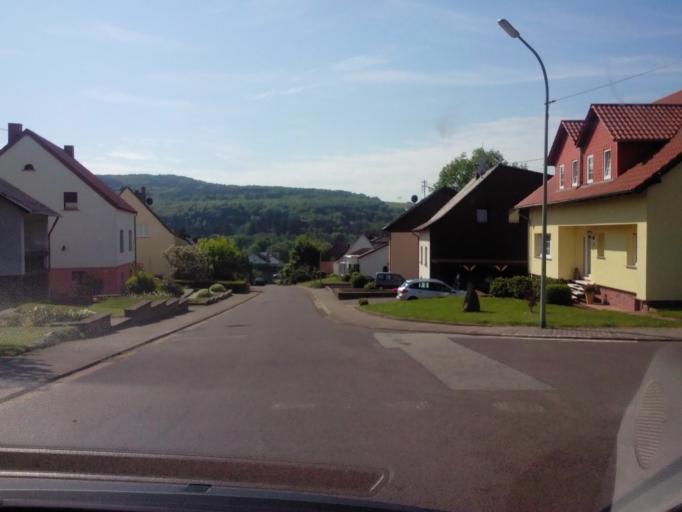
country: DE
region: Saarland
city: Schmelz
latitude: 49.3967
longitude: 6.8404
